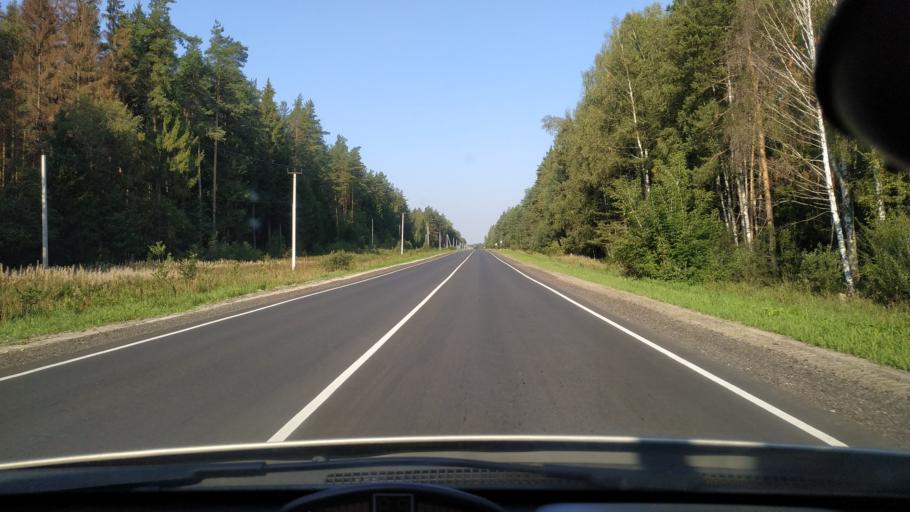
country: RU
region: Moskovskaya
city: Misheronskiy
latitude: 55.6576
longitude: 39.7908
